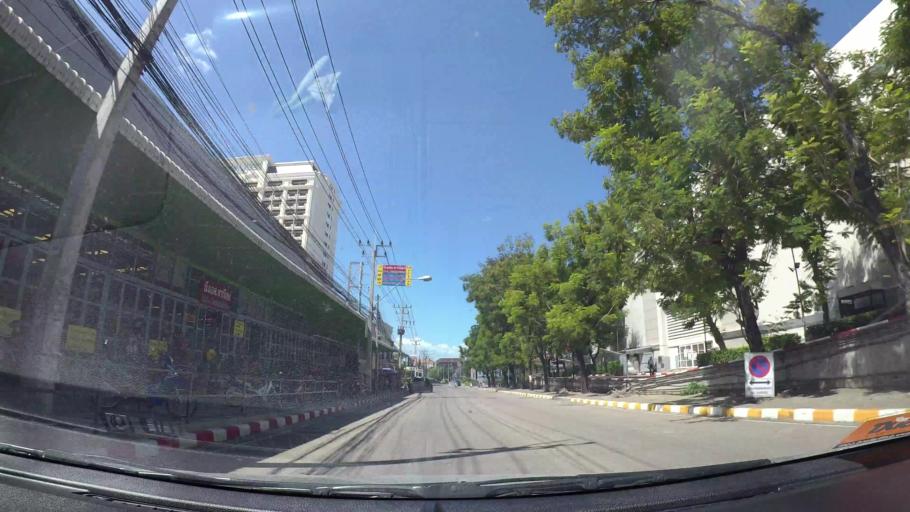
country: TH
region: Chon Buri
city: Phatthaya
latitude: 12.9458
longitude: 100.8918
